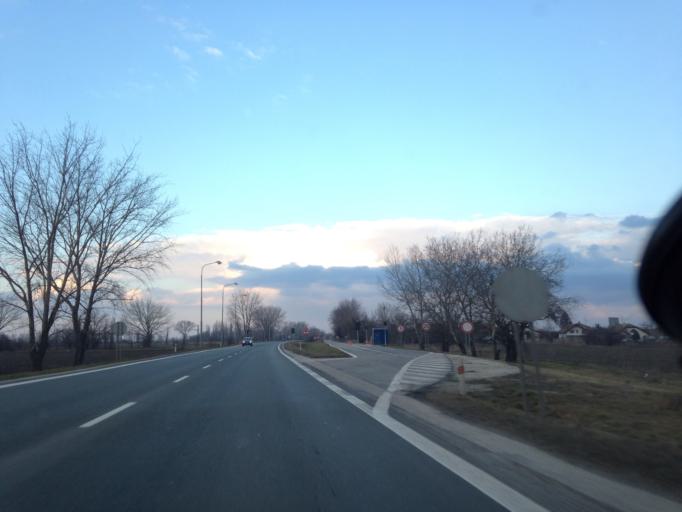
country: SK
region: Nitriansky
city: Komarno
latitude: 47.7828
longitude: 18.1639
